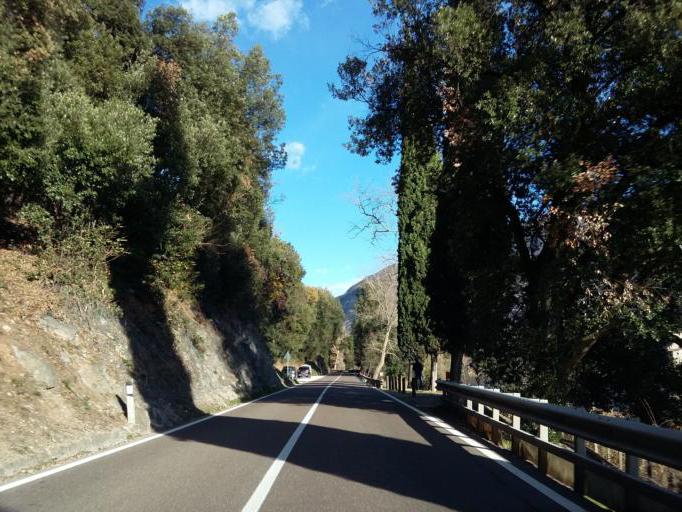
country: IT
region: Trentino-Alto Adige
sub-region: Provincia di Trento
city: Padergnone
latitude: 46.0547
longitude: 10.9605
